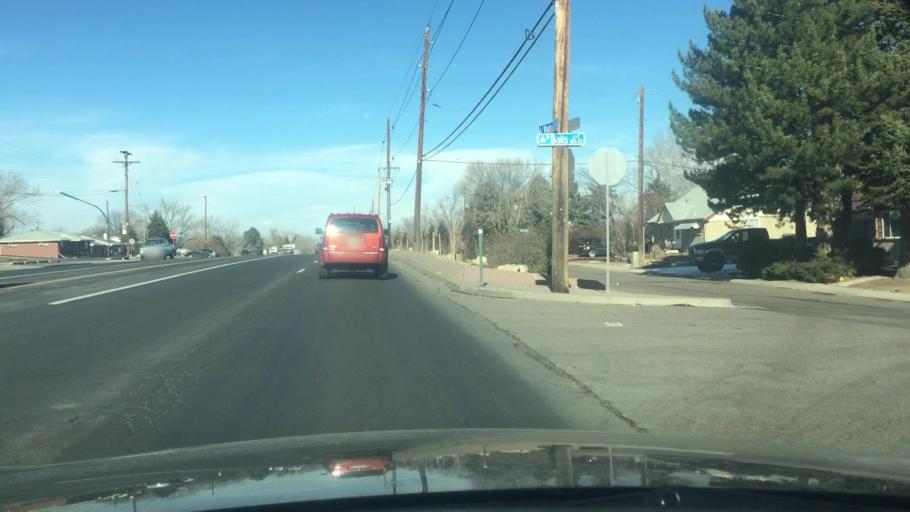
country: US
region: Colorado
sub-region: Jefferson County
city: Lakewood
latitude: 39.6848
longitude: -105.0814
